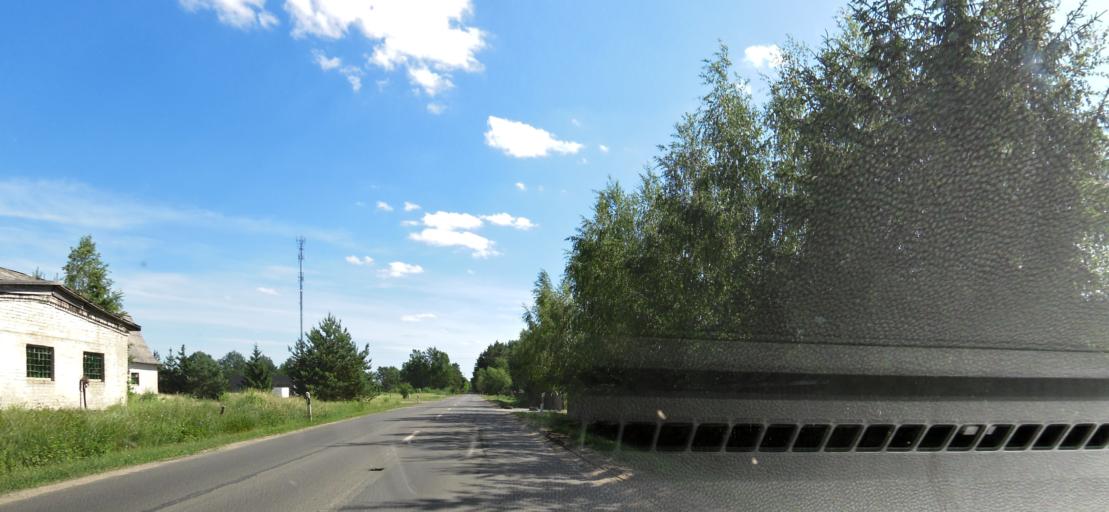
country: LT
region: Vilnius County
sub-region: Vilnius
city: Fabijoniskes
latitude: 54.7998
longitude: 25.3485
